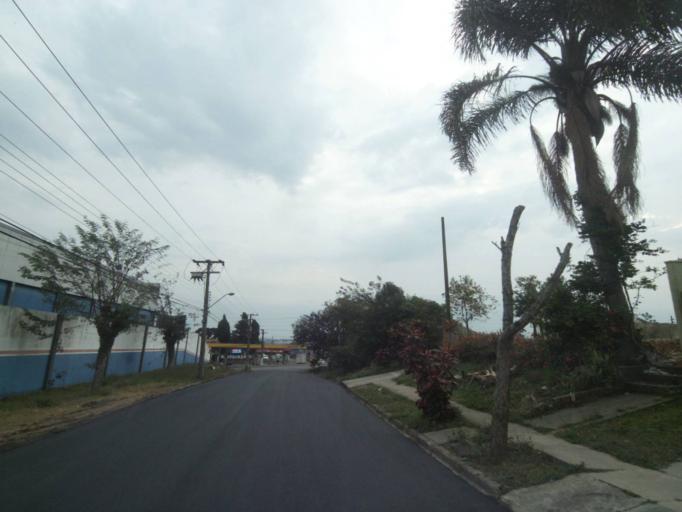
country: BR
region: Parana
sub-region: Pinhais
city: Pinhais
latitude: -25.4727
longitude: -49.2337
